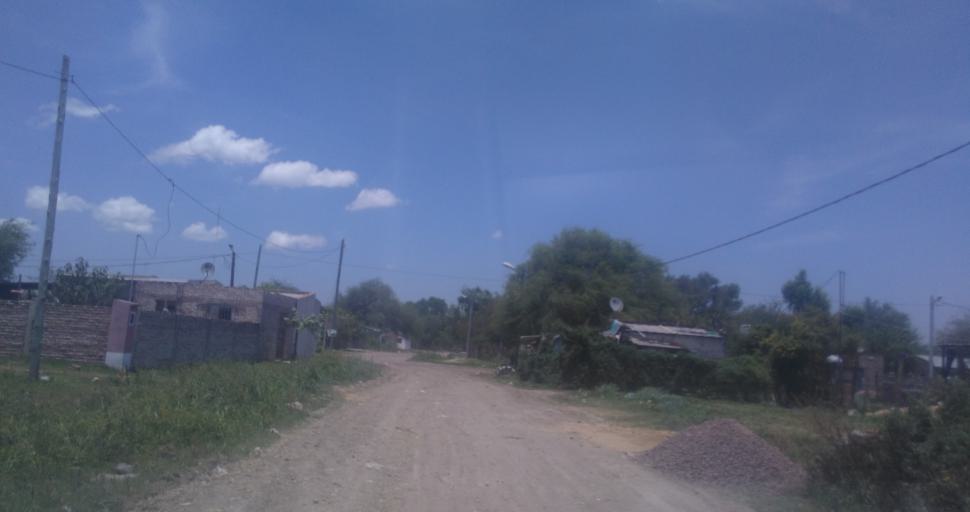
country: AR
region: Chaco
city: Fontana
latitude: -27.4224
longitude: -59.0404
